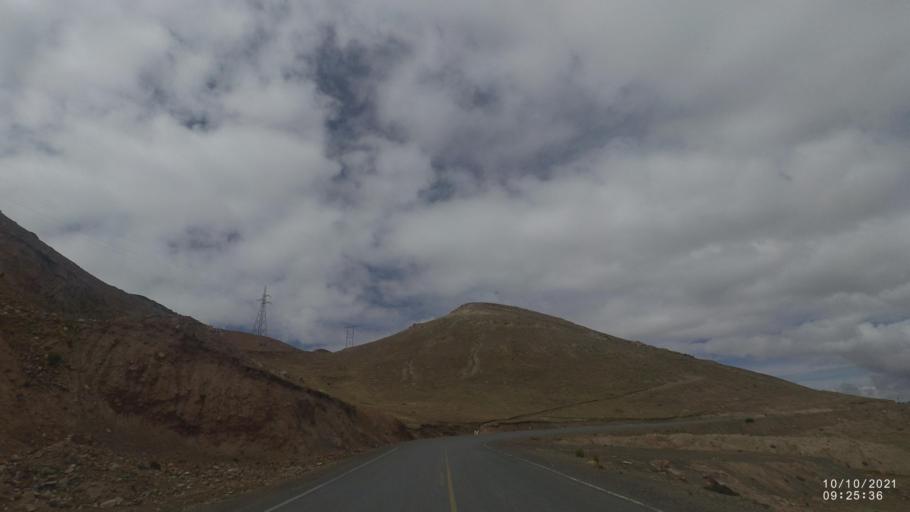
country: BO
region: La Paz
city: Quime
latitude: -17.0924
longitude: -67.3168
